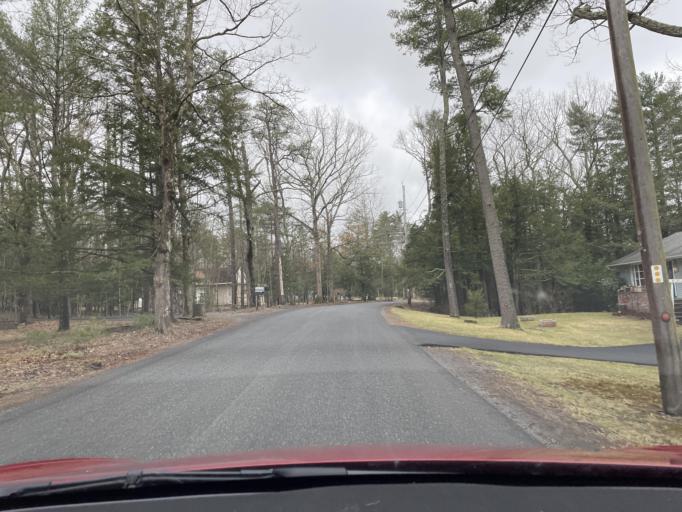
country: US
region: New York
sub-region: Ulster County
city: Manorville
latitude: 42.0932
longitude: -74.0356
